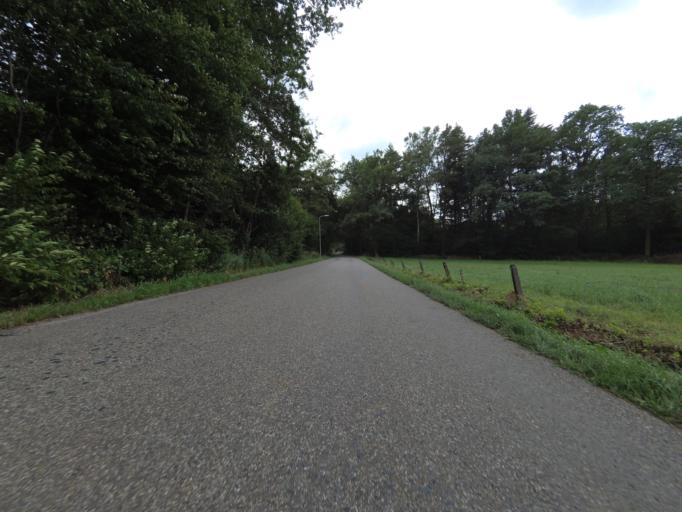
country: NL
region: Overijssel
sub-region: Gemeente Hengelo
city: Hengelo
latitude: 52.2576
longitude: 6.8403
